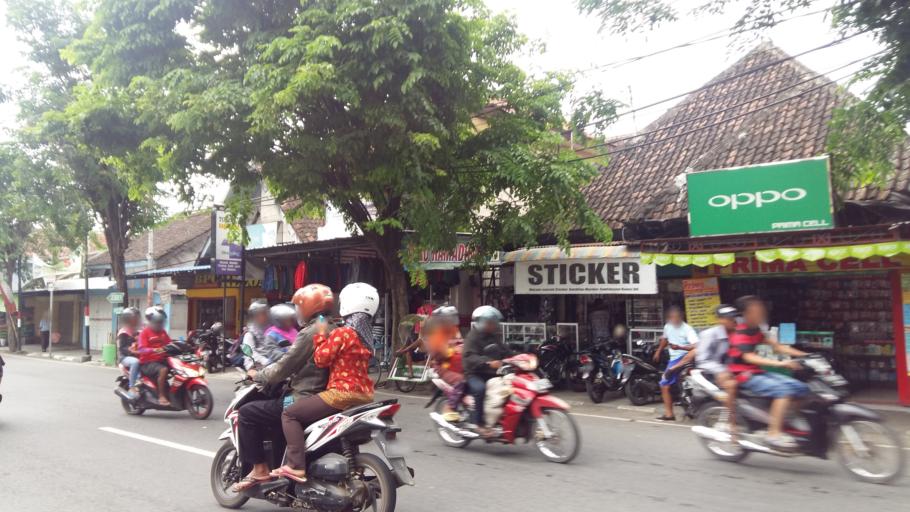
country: ID
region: East Java
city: Krajan
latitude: -8.3099
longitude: 114.2920
